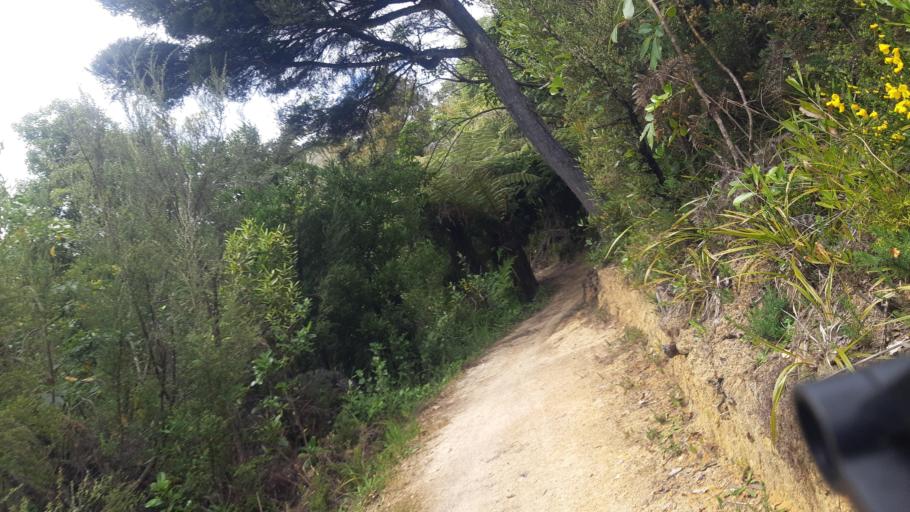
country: NZ
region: Marlborough
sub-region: Marlborough District
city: Picton
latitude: -41.2661
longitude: 173.9975
